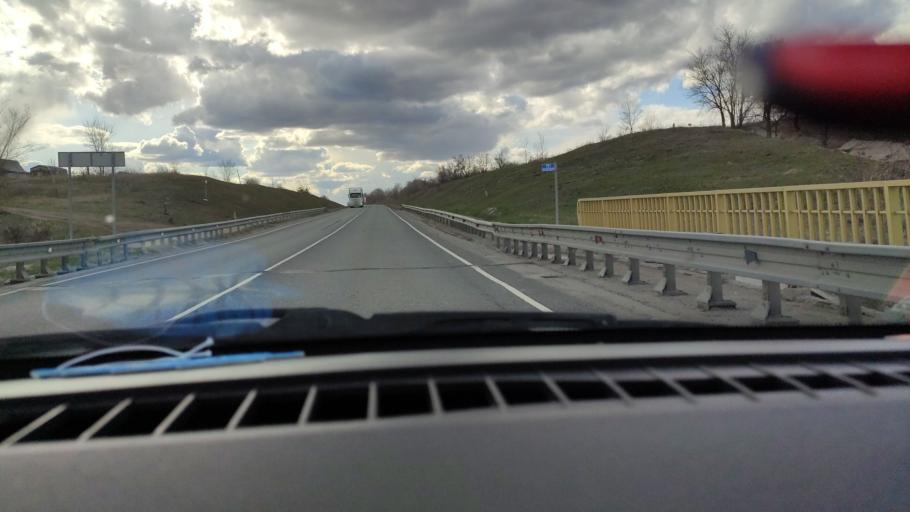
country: RU
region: Saratov
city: Tersa
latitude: 52.0839
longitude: 47.5817
